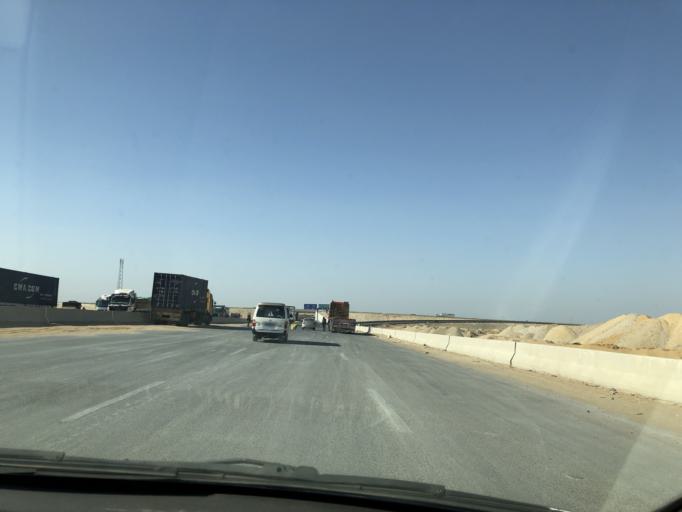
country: EG
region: Muhafazat al Minufiyah
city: Ashmun
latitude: 30.0634
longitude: 30.8459
